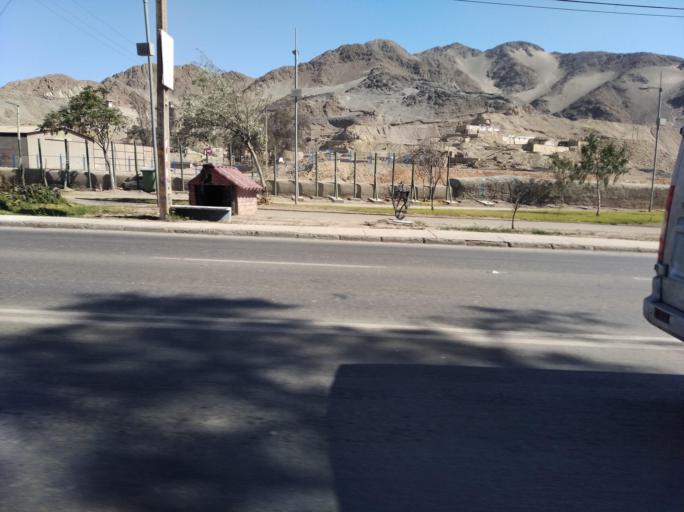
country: CL
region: Atacama
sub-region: Provincia de Copiapo
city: Copiapo
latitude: -27.3651
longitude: -70.3415
